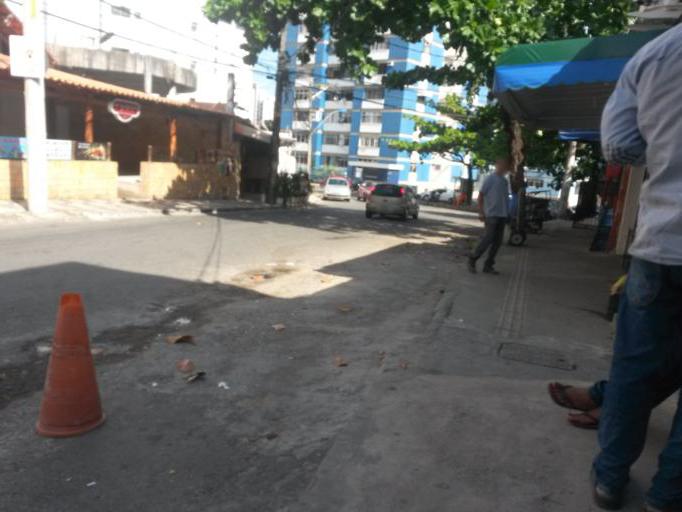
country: BR
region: Bahia
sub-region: Salvador
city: Salvador
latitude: -13.0011
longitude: -38.4619
